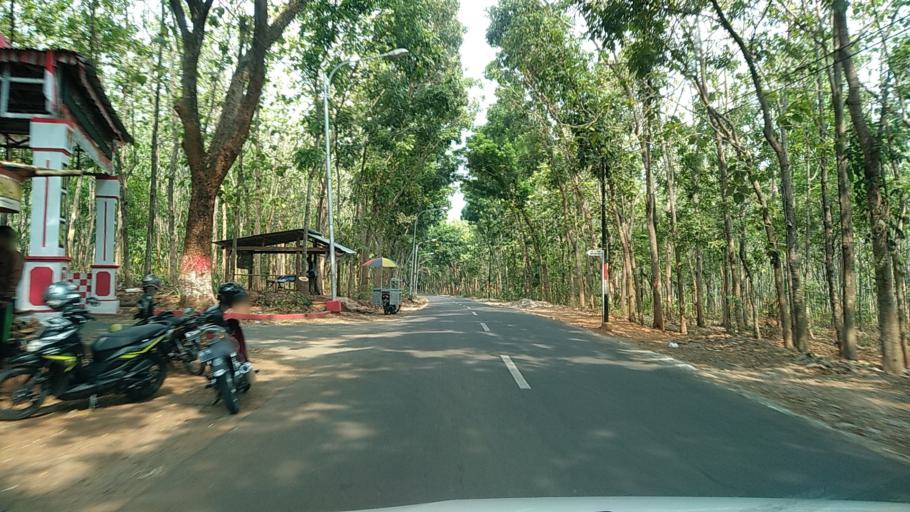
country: ID
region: Central Java
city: Semarang
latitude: -7.0016
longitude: 110.3073
